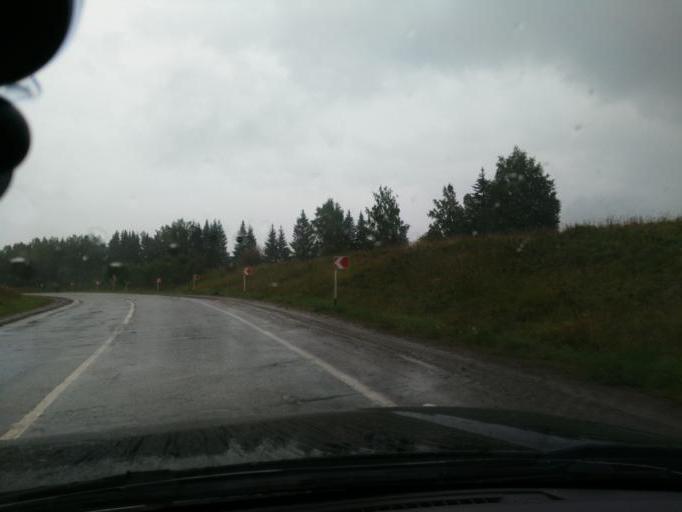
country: RU
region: Perm
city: Osa
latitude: 57.2908
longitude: 55.6077
